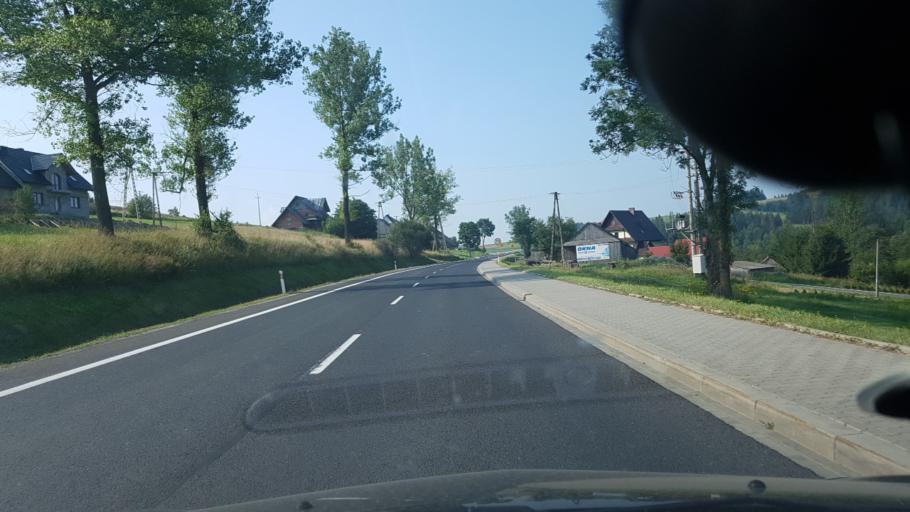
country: PL
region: Lesser Poland Voivodeship
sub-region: Powiat nowotarski
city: Podwilk
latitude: 49.5305
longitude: 19.7142
